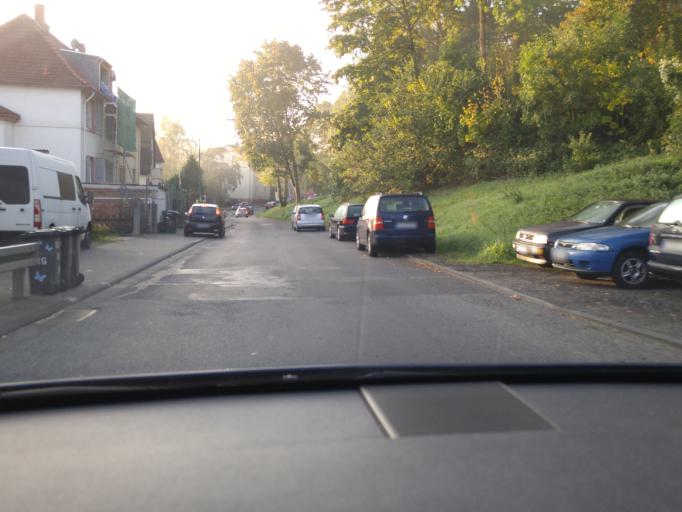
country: DE
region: Hesse
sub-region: Regierungsbezirk Darmstadt
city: Friedberg
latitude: 50.3427
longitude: 8.7552
